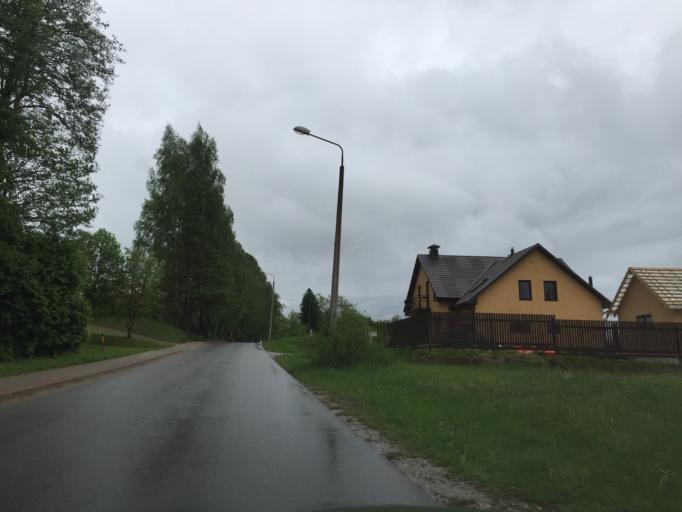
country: LV
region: Kegums
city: Kegums
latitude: 56.7479
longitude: 24.7195
